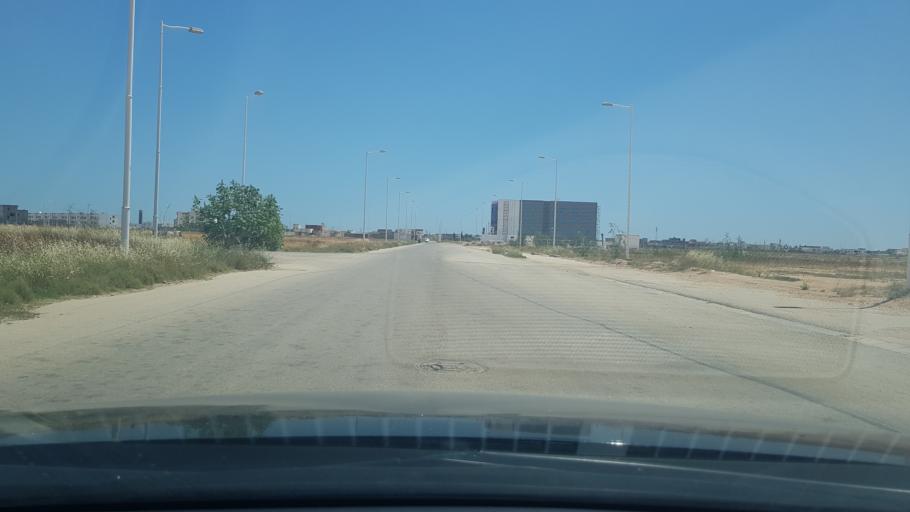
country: TN
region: Safaqis
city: Al Qarmadah
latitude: 34.8341
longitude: 10.7461
